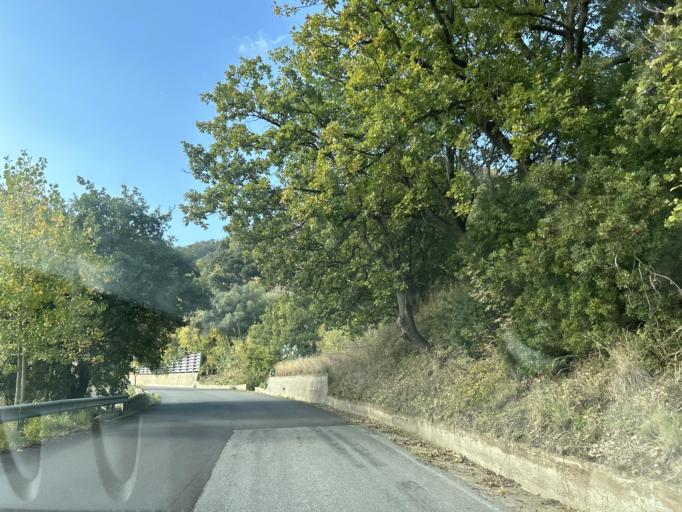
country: IT
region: Calabria
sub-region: Provincia di Catanzaro
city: Gasperina
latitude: 38.7275
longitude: 16.5135
